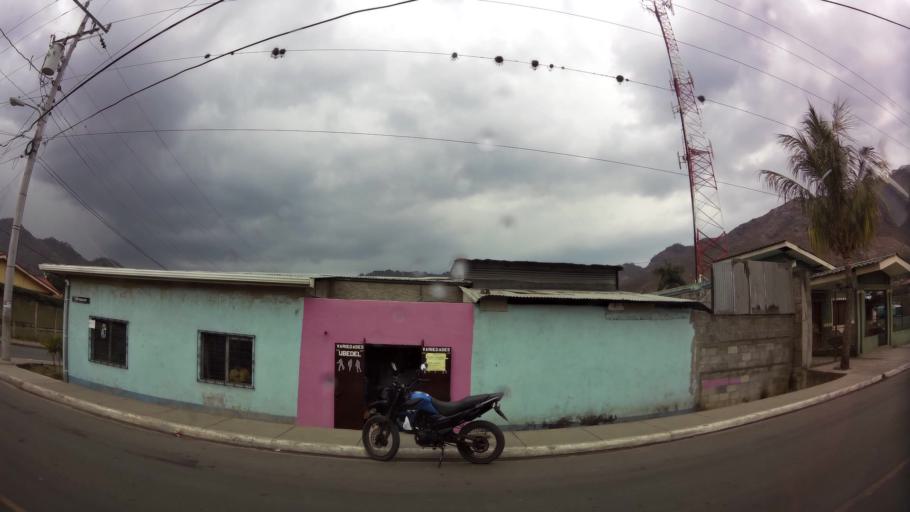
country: NI
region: Jinotega
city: Jinotega
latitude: 13.0913
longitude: -85.9981
